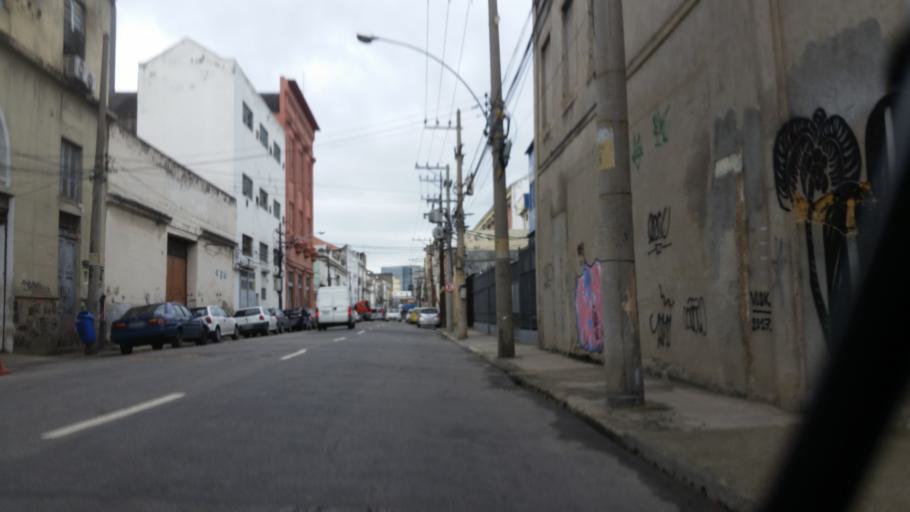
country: BR
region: Rio de Janeiro
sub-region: Rio De Janeiro
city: Rio de Janeiro
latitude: -22.9052
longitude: -43.2072
